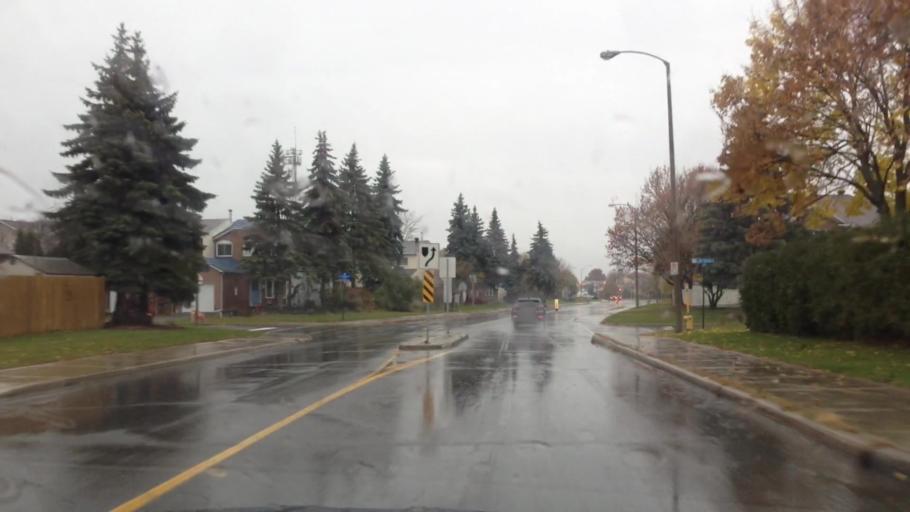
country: CA
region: Ontario
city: Clarence-Rockland
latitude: 45.4659
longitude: -75.4863
